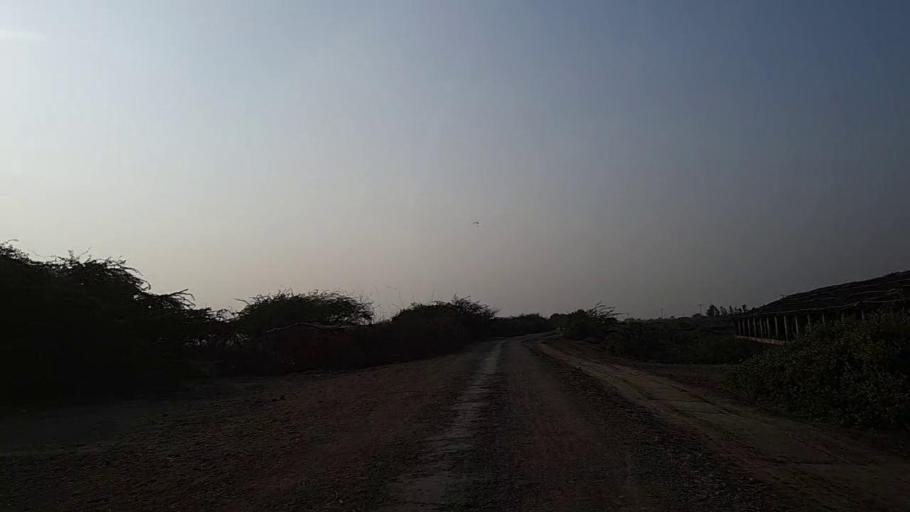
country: PK
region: Sindh
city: Thatta
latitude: 24.6918
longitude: 67.7915
